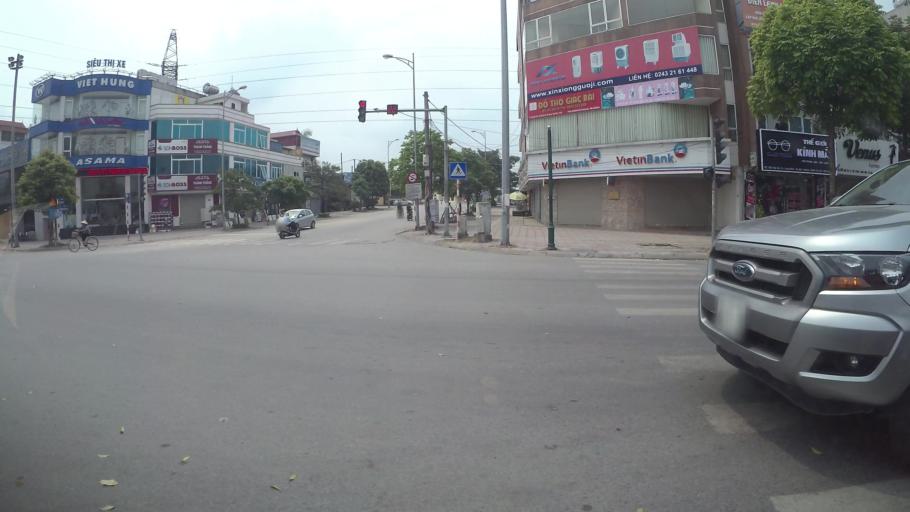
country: VN
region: Ha Noi
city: Trau Quy
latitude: 21.0699
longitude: 105.9022
